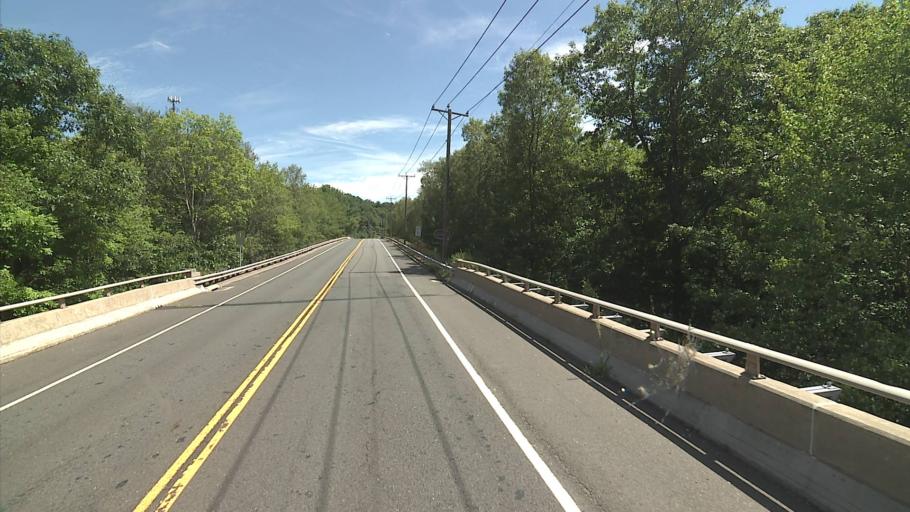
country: US
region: Connecticut
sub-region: Tolland County
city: South Coventry
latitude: 41.8355
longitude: -72.3101
